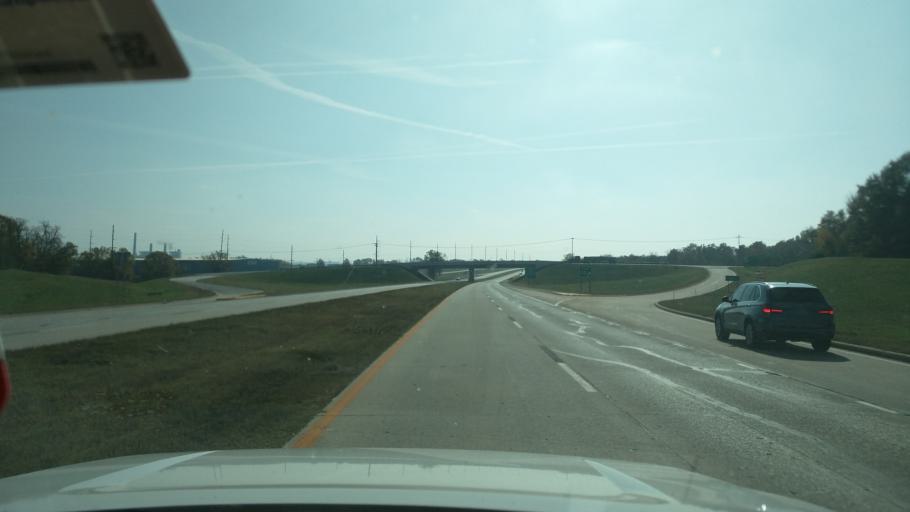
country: US
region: Oklahoma
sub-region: Muskogee County
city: Fort Gibson
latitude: 35.7868
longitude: -95.3116
